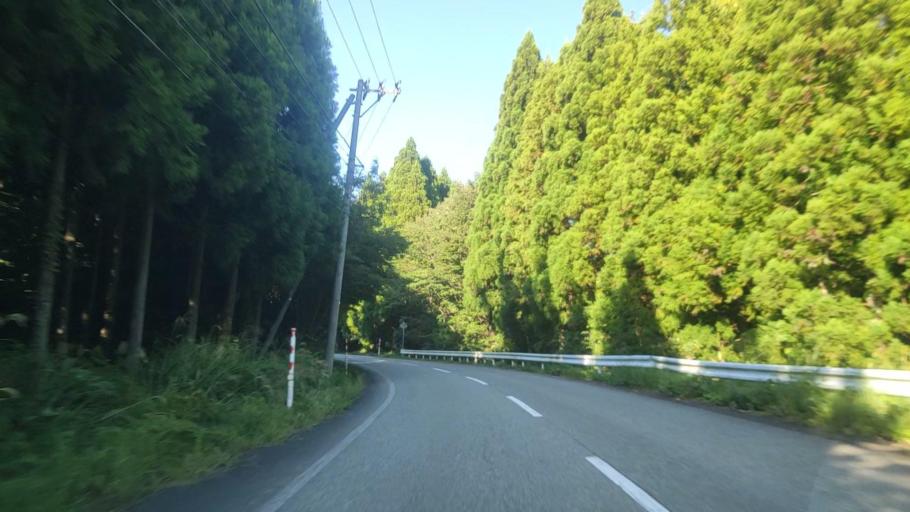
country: JP
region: Ishikawa
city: Nanao
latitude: 37.1126
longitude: 136.9641
